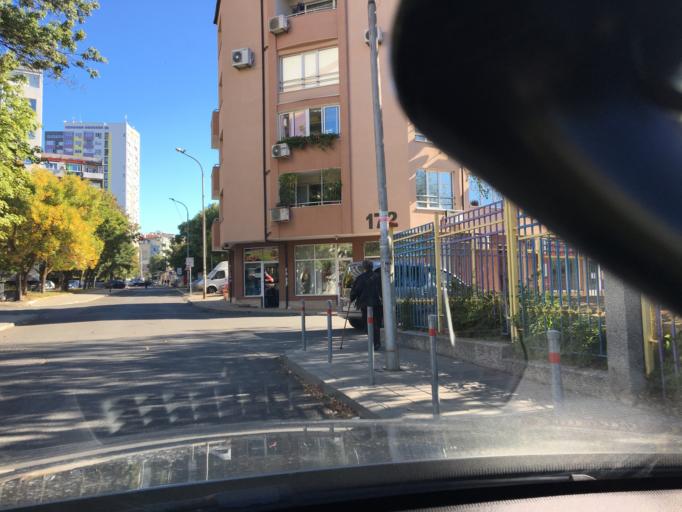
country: BG
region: Burgas
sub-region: Obshtina Burgas
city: Burgas
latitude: 42.5191
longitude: 27.4478
